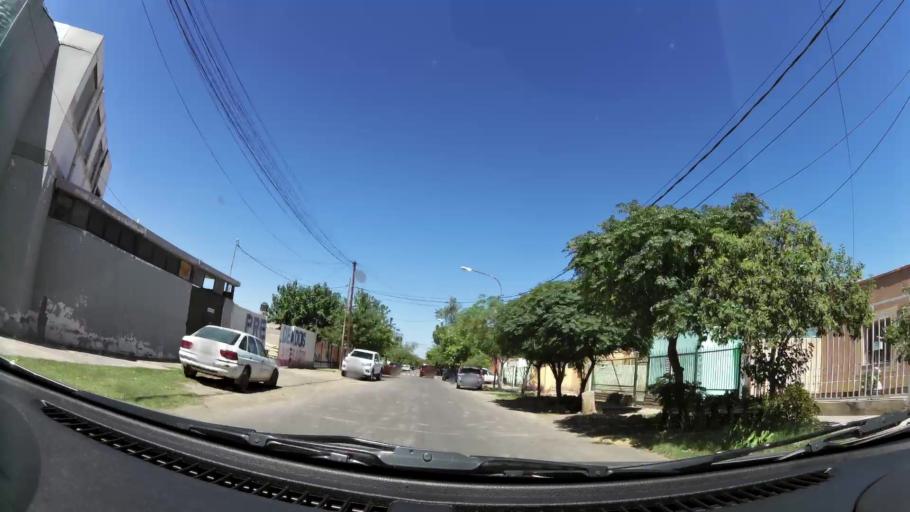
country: AR
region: San Juan
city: San Juan
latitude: -31.5167
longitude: -68.5207
